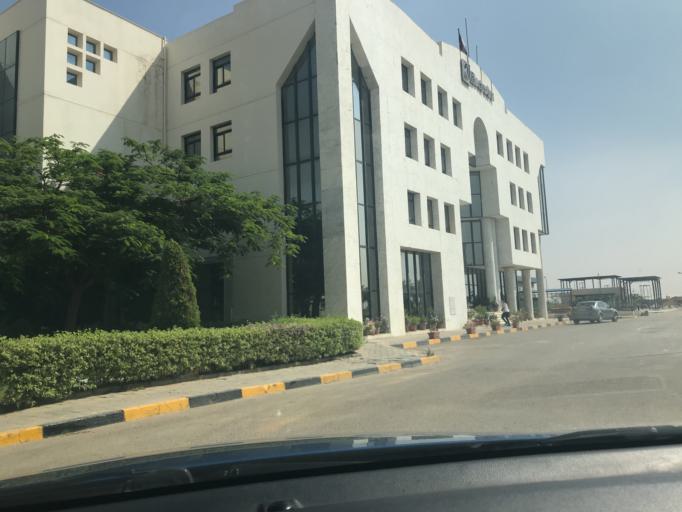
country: EG
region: Eastern Province
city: Bilbays
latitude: 30.2474
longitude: 31.7585
